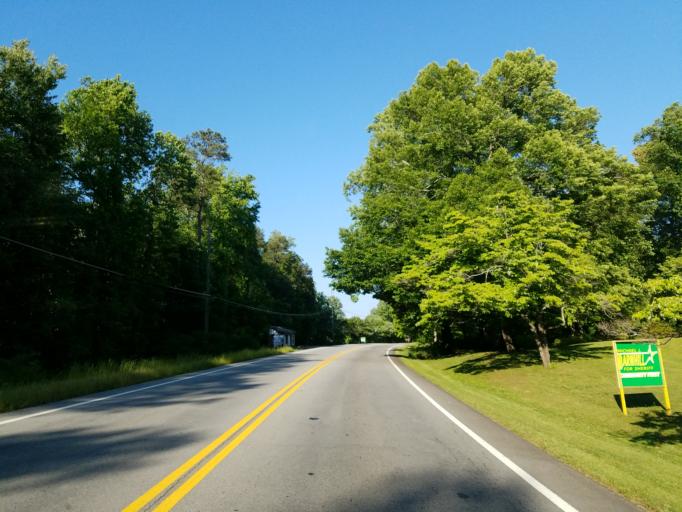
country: US
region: Georgia
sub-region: Carroll County
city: Villa Rica
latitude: 33.7338
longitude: -84.8667
